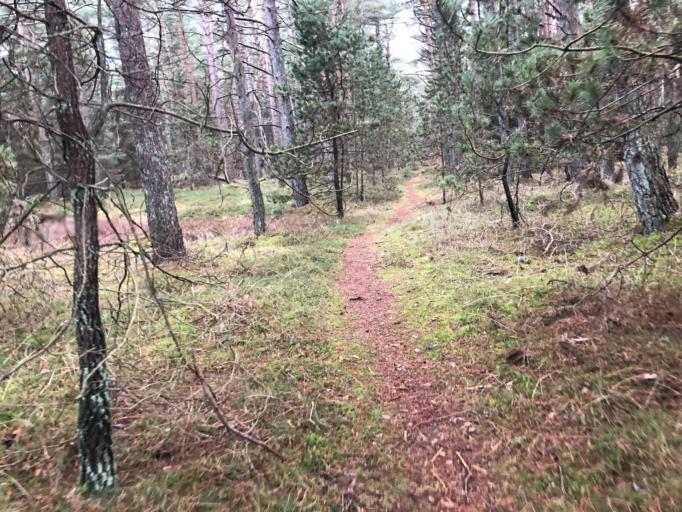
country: DK
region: Central Jutland
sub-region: Holstebro Kommune
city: Ulfborg
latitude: 56.2915
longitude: 8.1686
